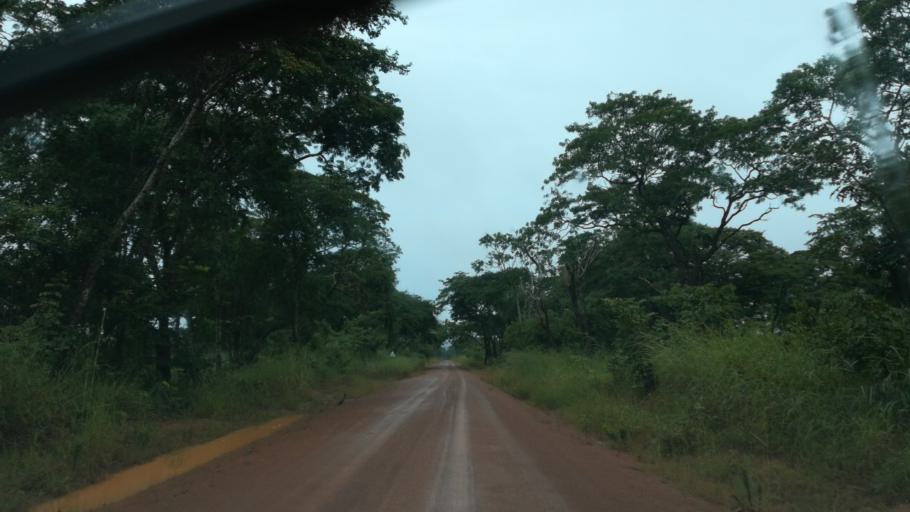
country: ZM
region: Luapula
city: Mwense
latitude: -10.7253
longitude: 28.2193
